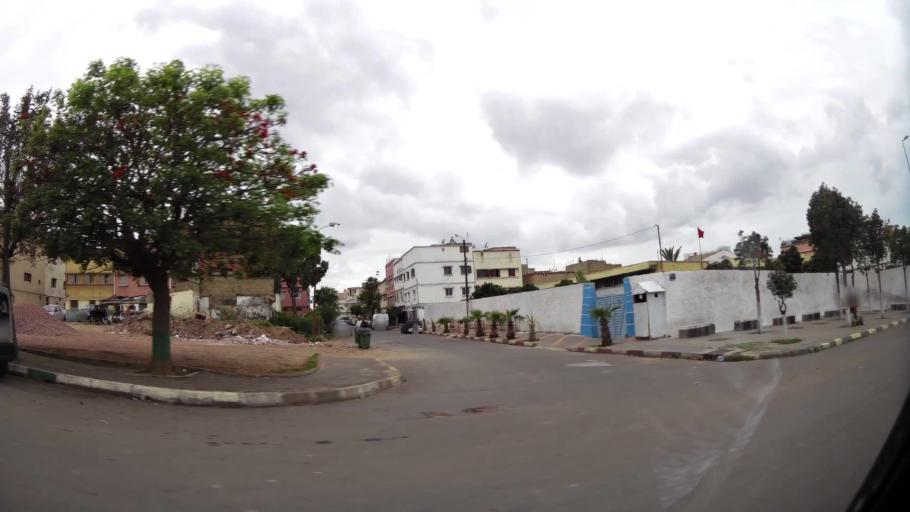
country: MA
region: Grand Casablanca
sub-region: Casablanca
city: Casablanca
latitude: 33.5695
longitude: -7.5668
